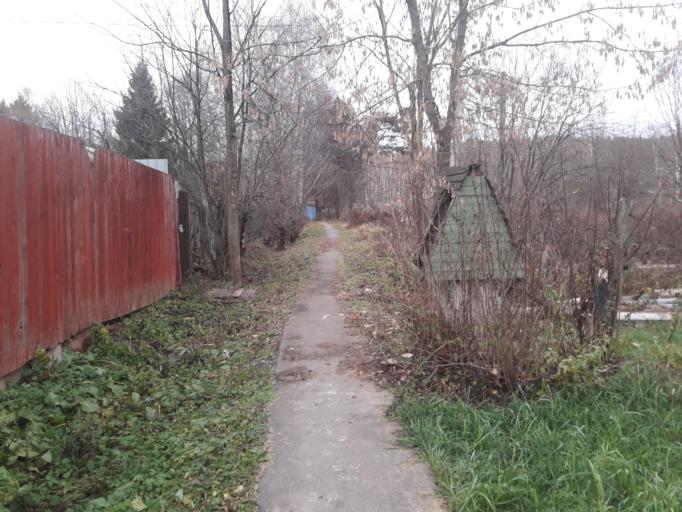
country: RU
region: Moskovskaya
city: Ashukino
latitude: 56.1674
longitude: 37.9629
